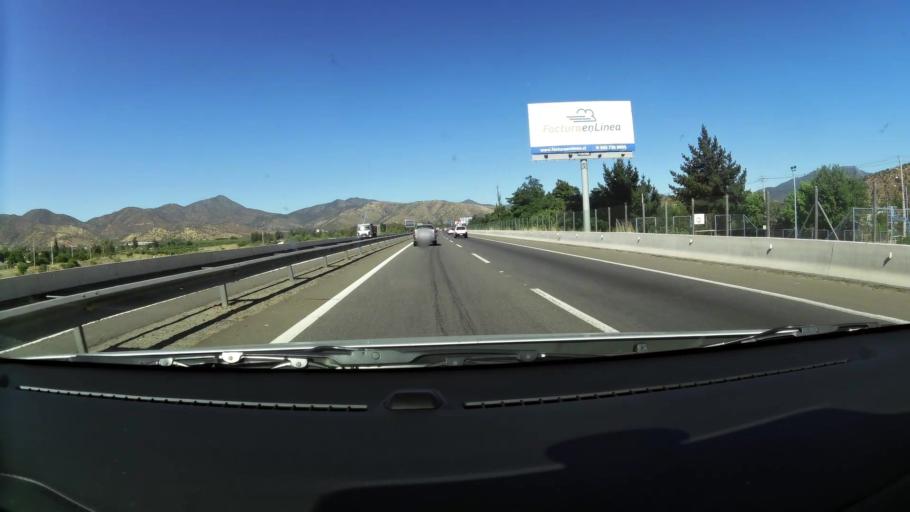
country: CL
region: Santiago Metropolitan
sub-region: Provincia de Melipilla
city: Melipilla
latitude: -33.4107
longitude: -71.1429
